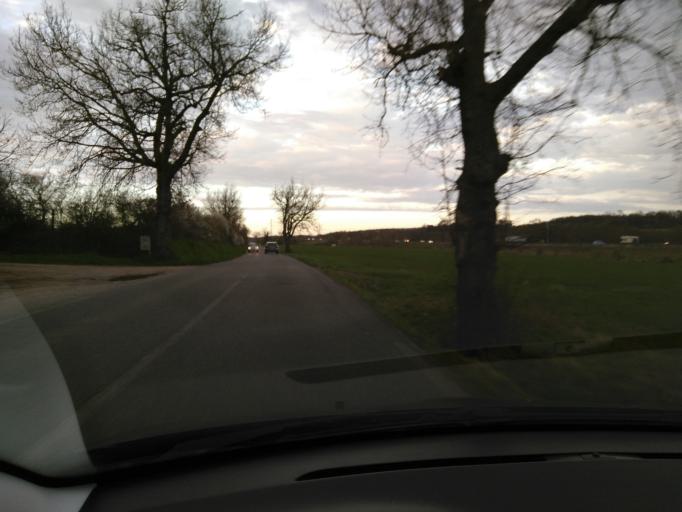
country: FR
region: Midi-Pyrenees
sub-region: Departement de la Haute-Garonne
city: La Salvetat-Saint-Gilles
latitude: 43.5902
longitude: 1.2723
